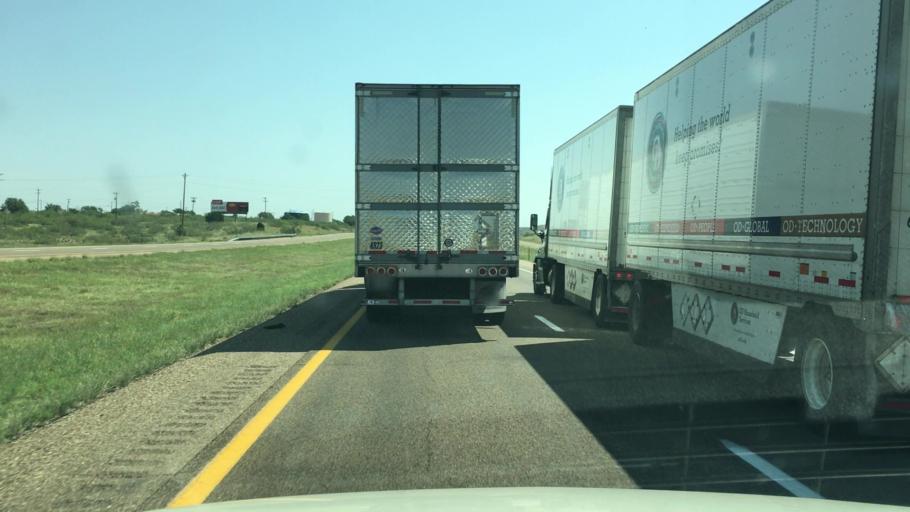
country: US
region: New Mexico
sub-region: Quay County
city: Tucumcari
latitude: 35.1457
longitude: -103.8046
